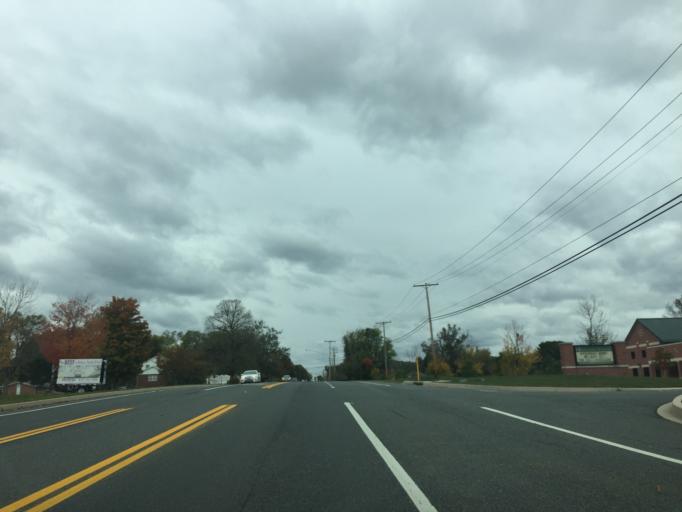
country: US
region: Maryland
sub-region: Harford County
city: Riverside
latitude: 39.4991
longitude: -76.2640
